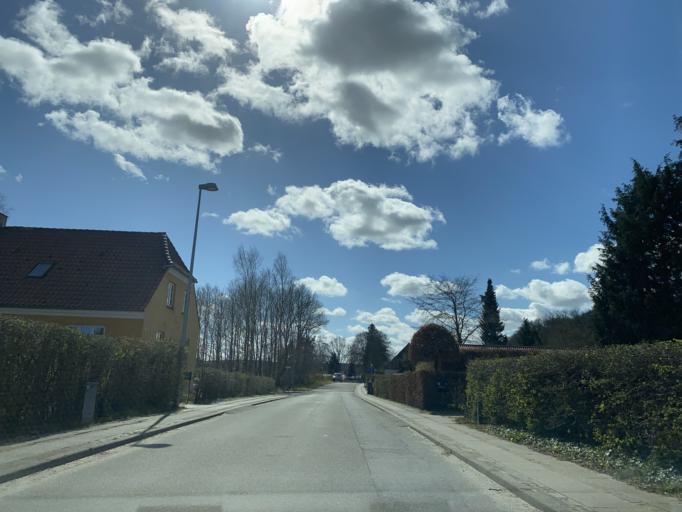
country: DK
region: Central Jutland
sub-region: Randers Kommune
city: Langa
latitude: 56.3866
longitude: 9.8903
